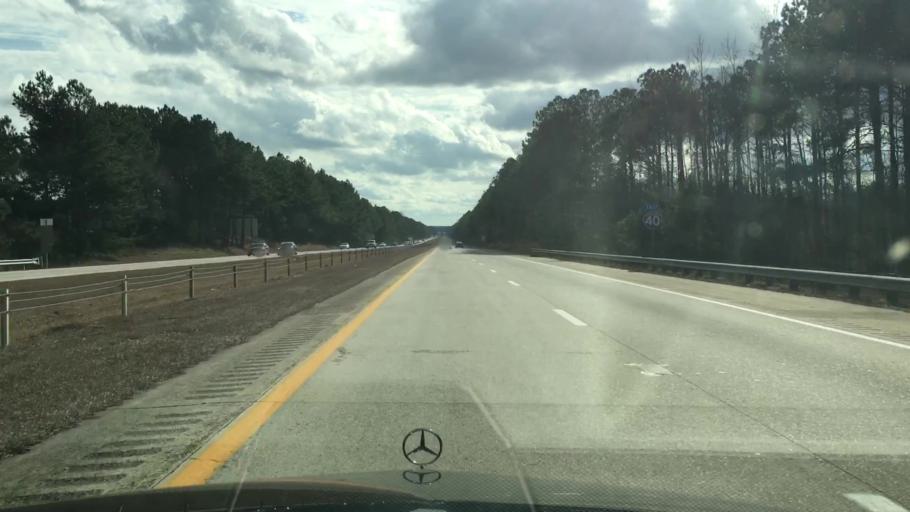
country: US
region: North Carolina
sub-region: Johnston County
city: Benson
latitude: 35.5093
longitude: -78.5557
